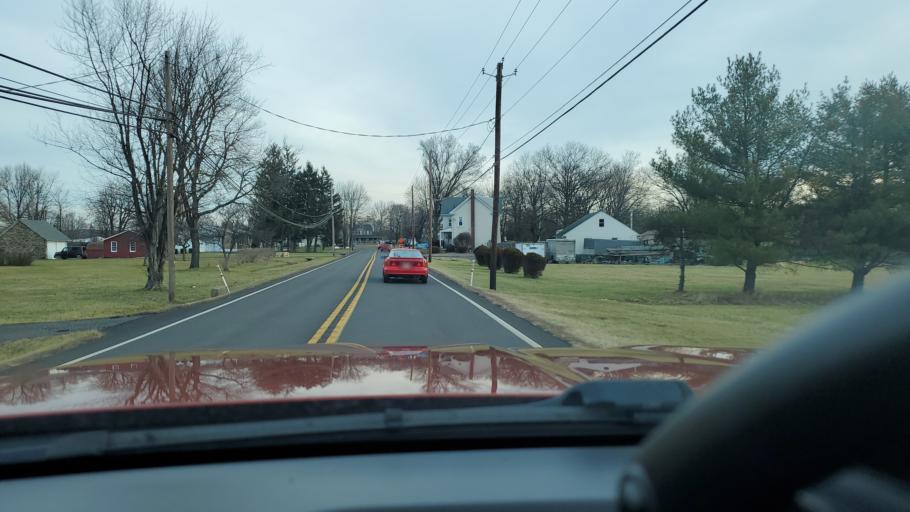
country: US
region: Pennsylvania
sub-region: Bucks County
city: Sellersville
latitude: 40.3626
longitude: -75.3373
